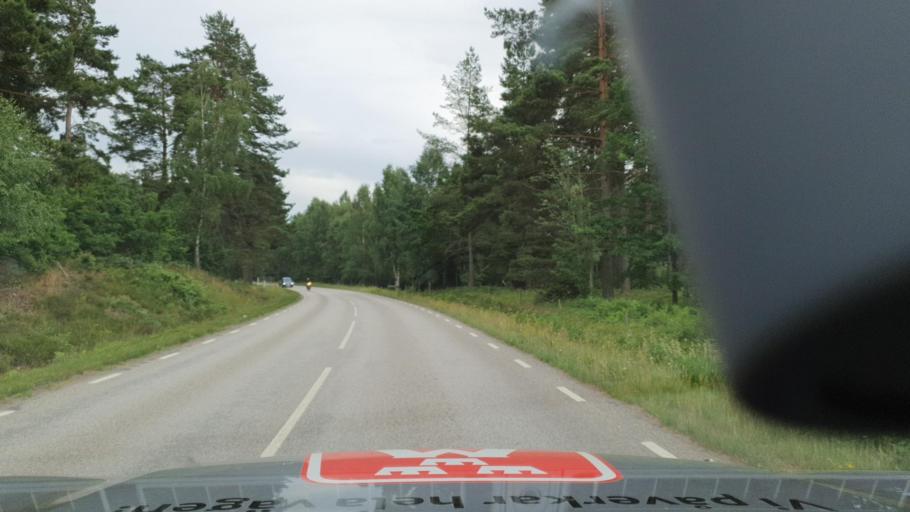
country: SE
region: Kalmar
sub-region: Nybro Kommun
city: Nybro
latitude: 56.6937
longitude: 15.9813
